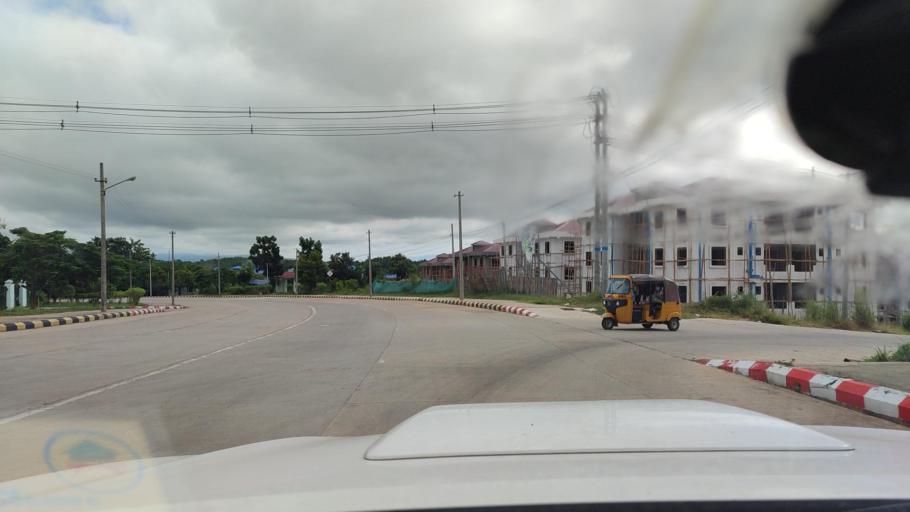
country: MM
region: Mandalay
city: Nay Pyi Taw
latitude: 19.7470
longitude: 96.0680
